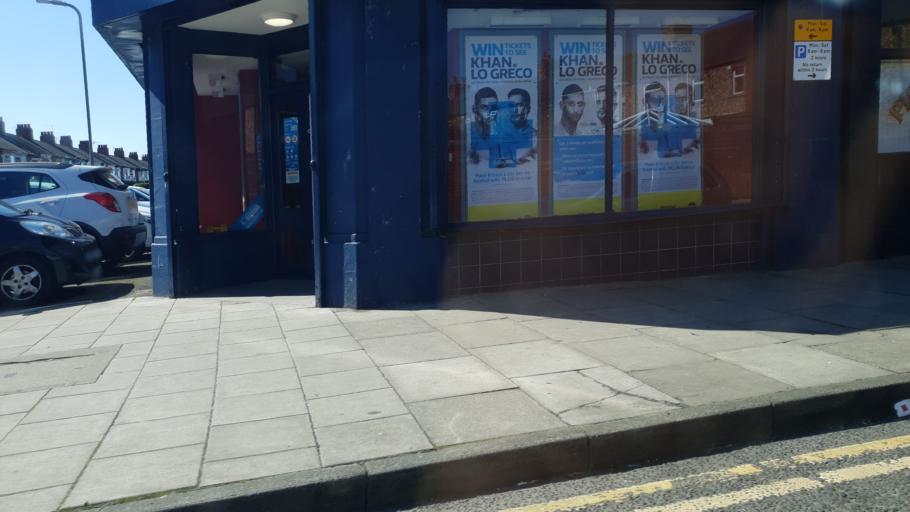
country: GB
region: England
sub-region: Middlesbrough
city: Middlesbrough
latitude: 54.5577
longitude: -1.2478
